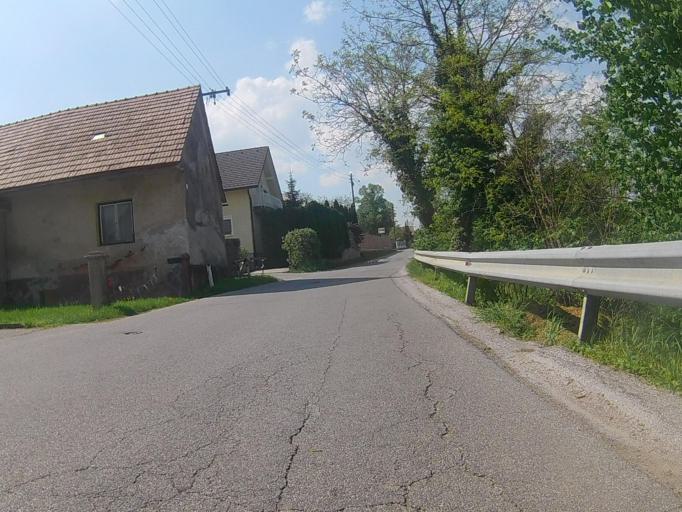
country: SI
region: Maribor
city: Maribor
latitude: 46.5527
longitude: 15.6810
